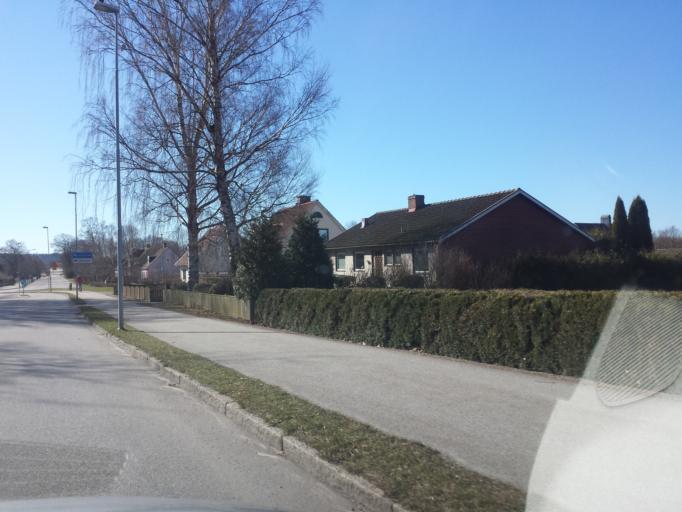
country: SE
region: Skane
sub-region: Sjobo Kommun
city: Sjoebo
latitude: 55.6425
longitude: 13.7048
